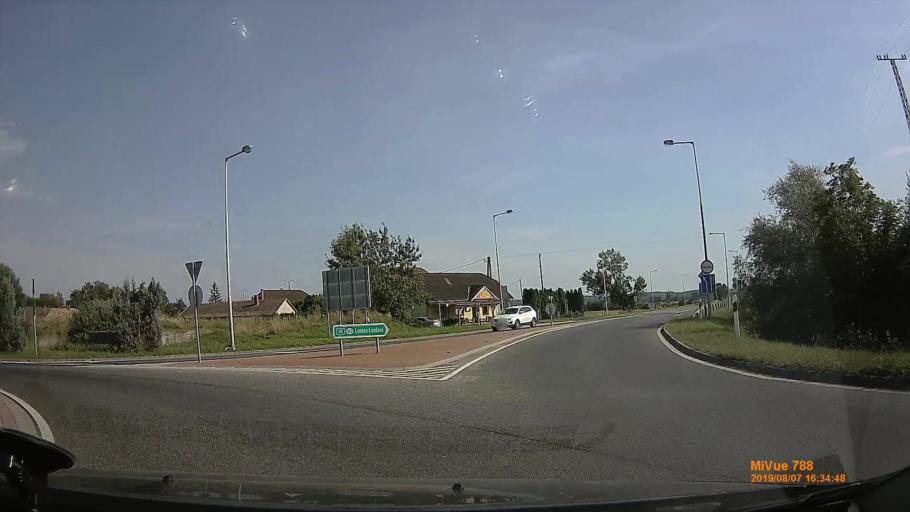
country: SI
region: Lendava-Lendva
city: Lendava
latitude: 46.6176
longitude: 16.4648
